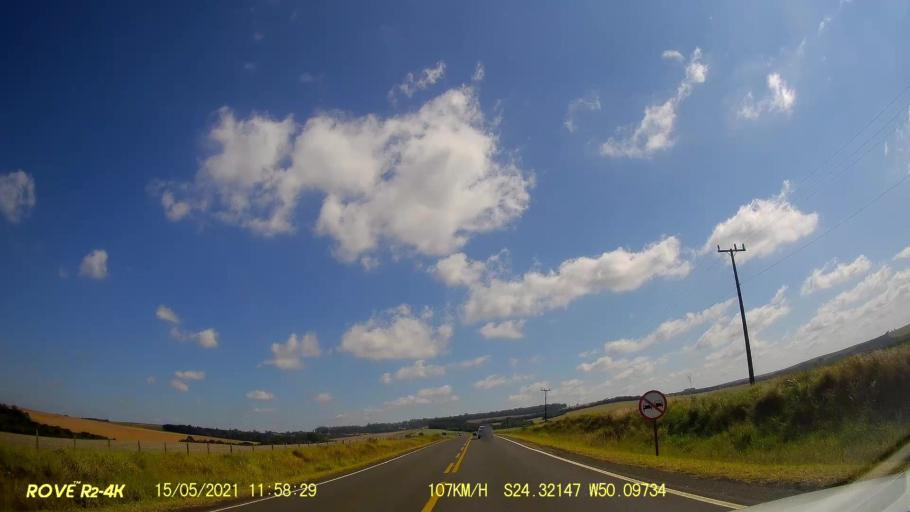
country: BR
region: Parana
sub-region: Pirai Do Sul
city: Pirai do Sul
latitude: -24.3217
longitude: -50.0976
